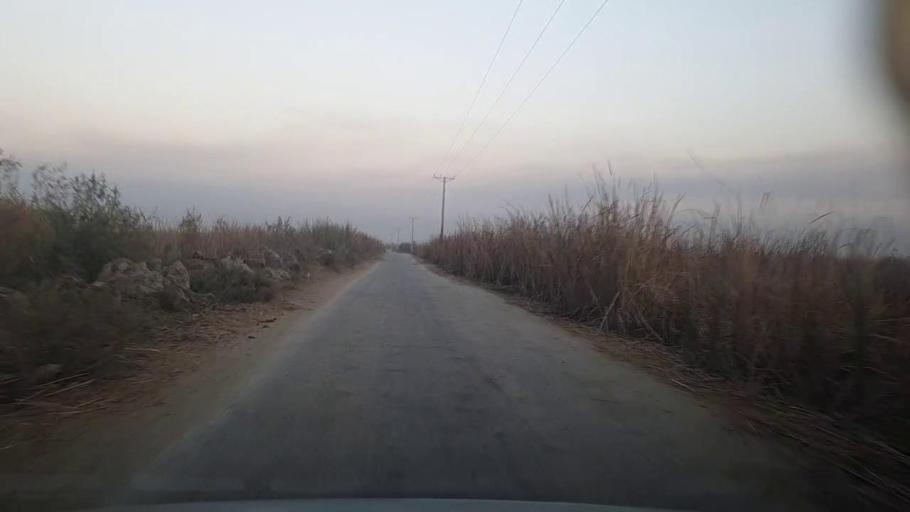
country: PK
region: Sindh
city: Kandiari
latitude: 26.6864
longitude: 68.9173
